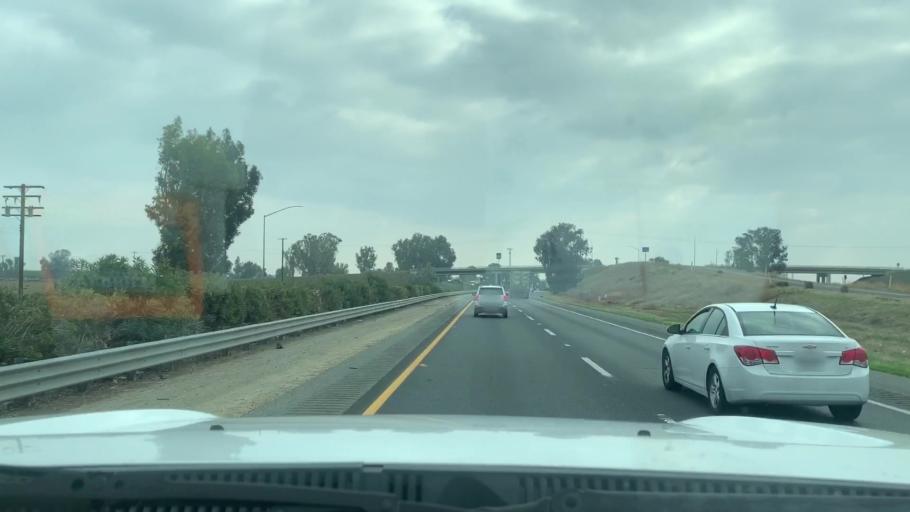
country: US
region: California
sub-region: Tulare County
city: Pixley
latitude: 36.0100
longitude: -119.3028
